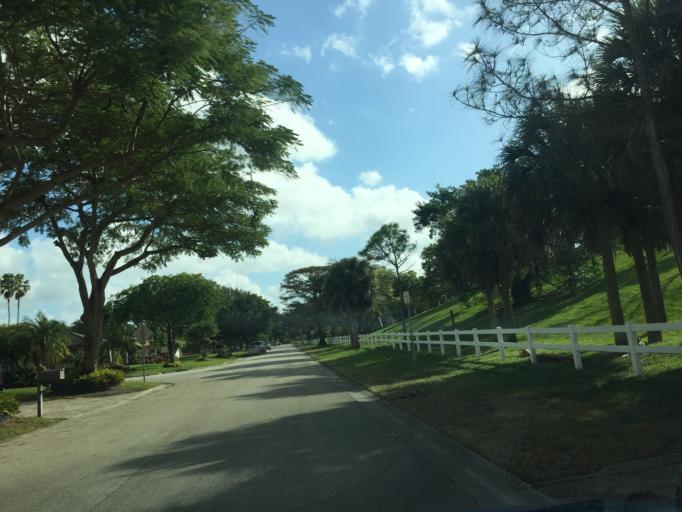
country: US
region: Florida
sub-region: Broward County
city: Tamarac
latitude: 26.2322
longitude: -80.2485
